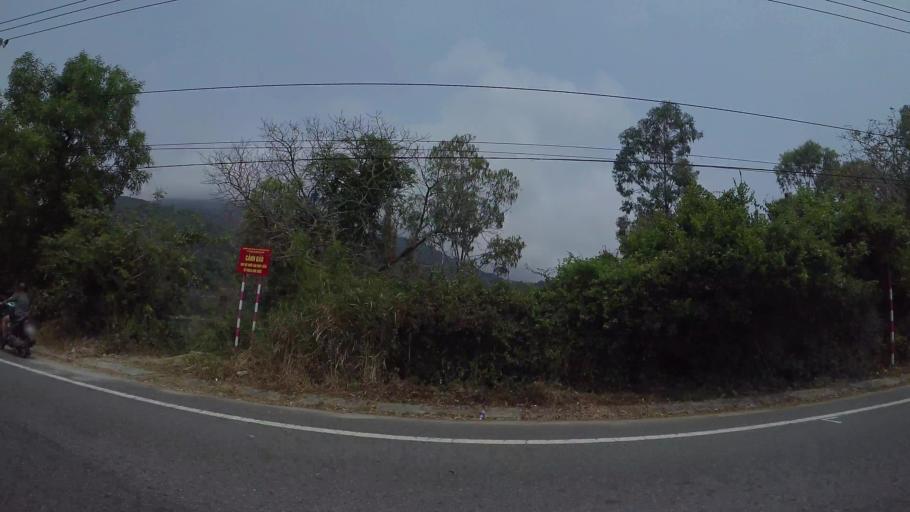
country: VN
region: Da Nang
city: Son Tra
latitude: 16.0979
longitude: 108.2673
